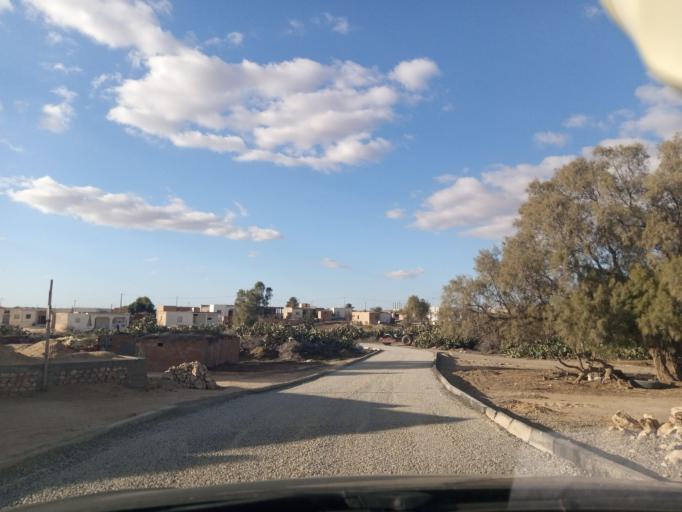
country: TN
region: Safaqis
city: Bi'r `Ali Bin Khalifah
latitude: 34.7104
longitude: 10.4237
